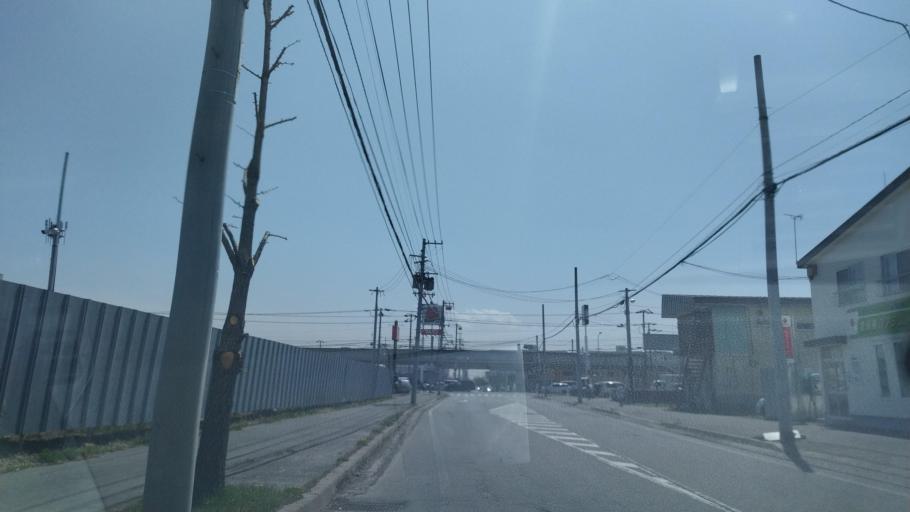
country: JP
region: Hokkaido
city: Obihiro
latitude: 42.9306
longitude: 143.1701
